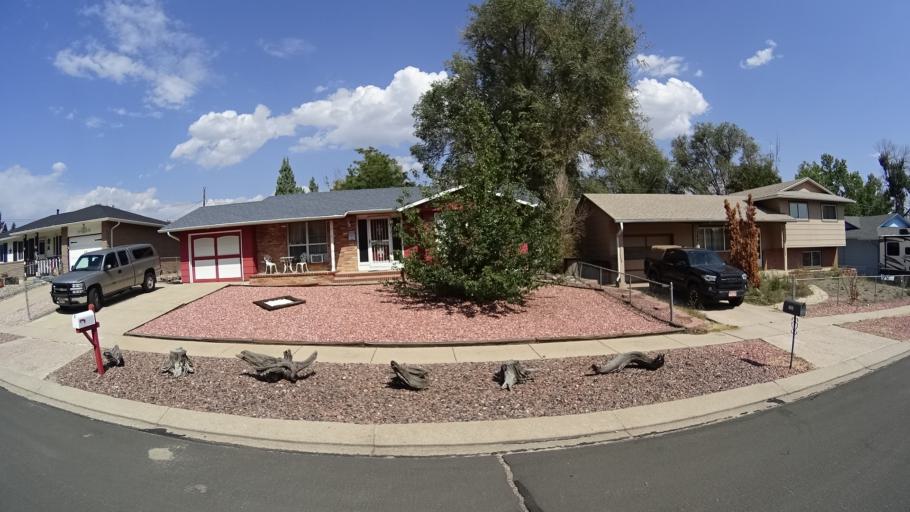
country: US
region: Colorado
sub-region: El Paso County
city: Colorado Springs
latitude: 38.8278
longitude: -104.7715
